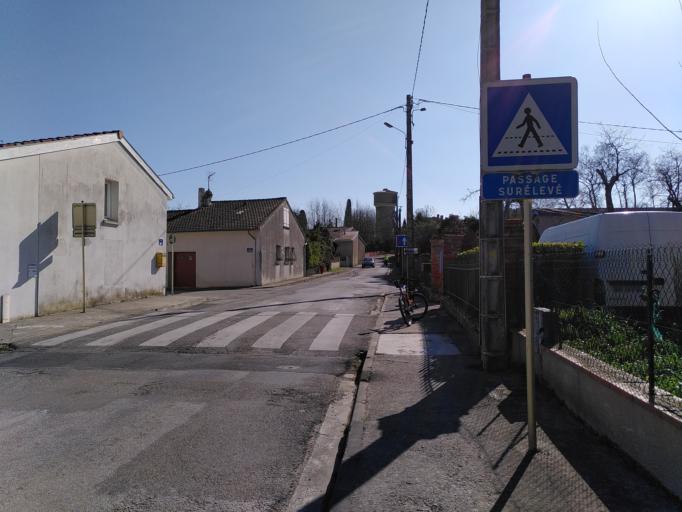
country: FR
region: Midi-Pyrenees
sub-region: Departement de la Haute-Garonne
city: Pompertuzat
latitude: 43.4794
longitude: 1.5261
